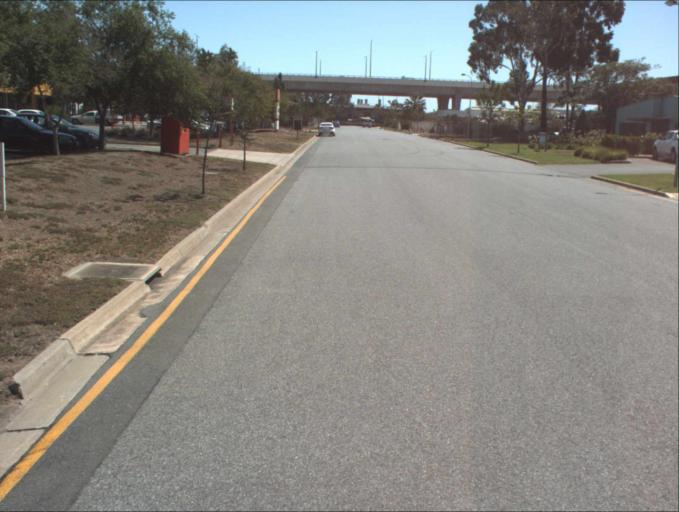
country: AU
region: South Australia
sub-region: Port Adelaide Enfield
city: Blair Athol
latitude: -34.8422
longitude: 138.5673
